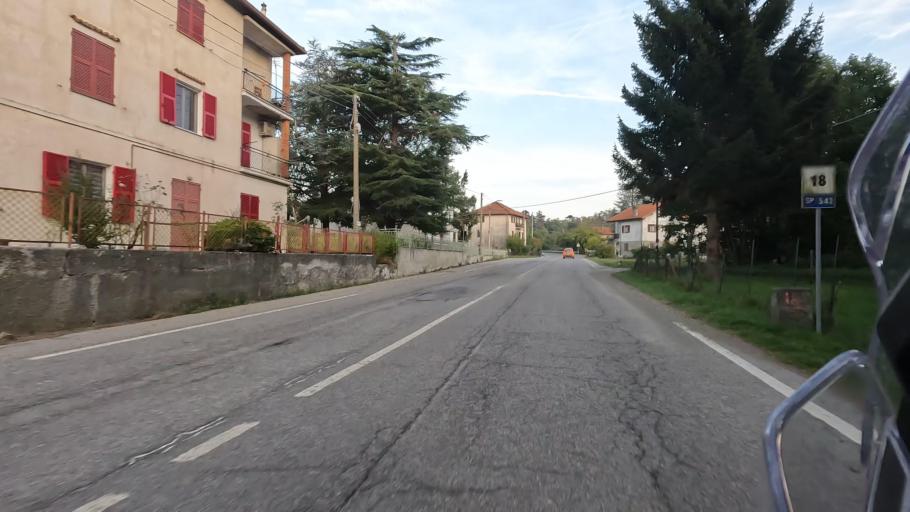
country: IT
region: Liguria
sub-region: Provincia di Savona
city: Osteria dei Cacciatori-Stella
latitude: 44.4295
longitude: 8.4682
